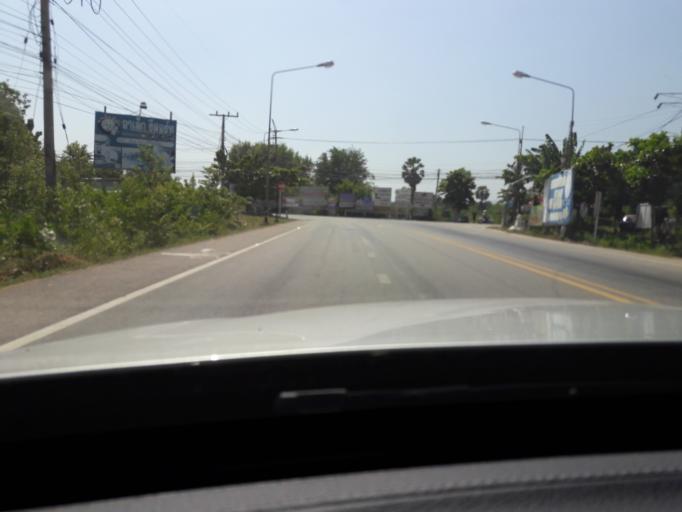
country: TH
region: Phetchaburi
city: Cha-am
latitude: 12.8253
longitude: 99.9842
